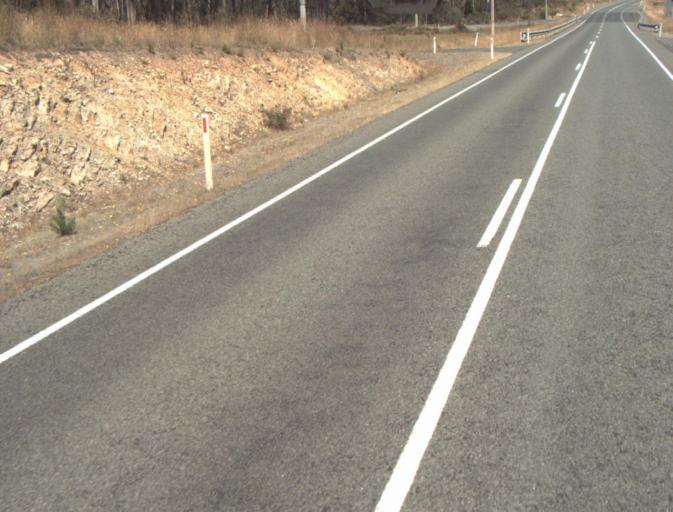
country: AU
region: Tasmania
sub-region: Launceston
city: Newstead
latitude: -41.3405
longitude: 147.3466
